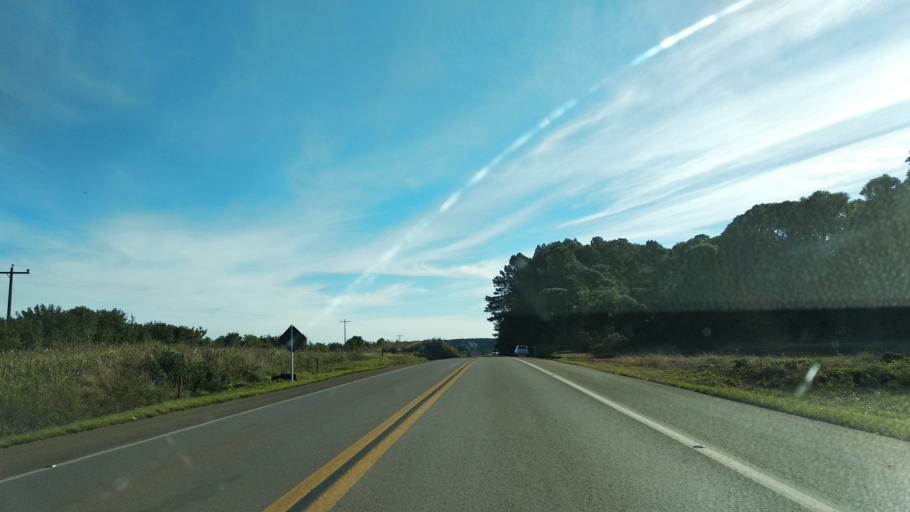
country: BR
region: Santa Catarina
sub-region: Celso Ramos
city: Celso Ramos
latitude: -27.5271
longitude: -51.3642
